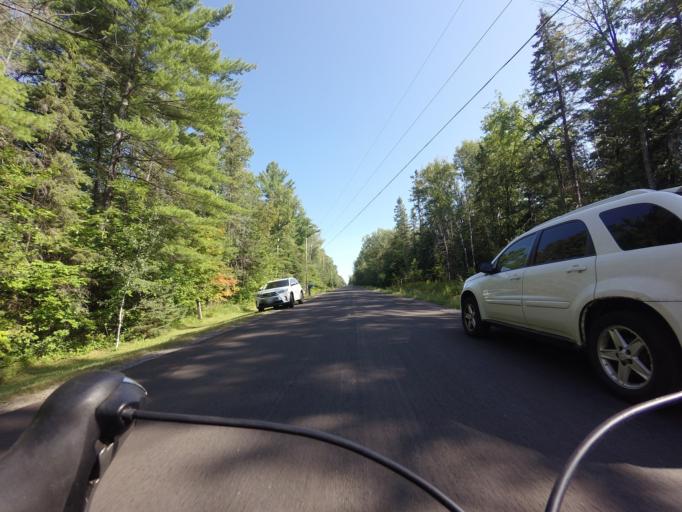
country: CA
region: Ontario
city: Bells Corners
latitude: 45.4634
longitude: -75.9796
